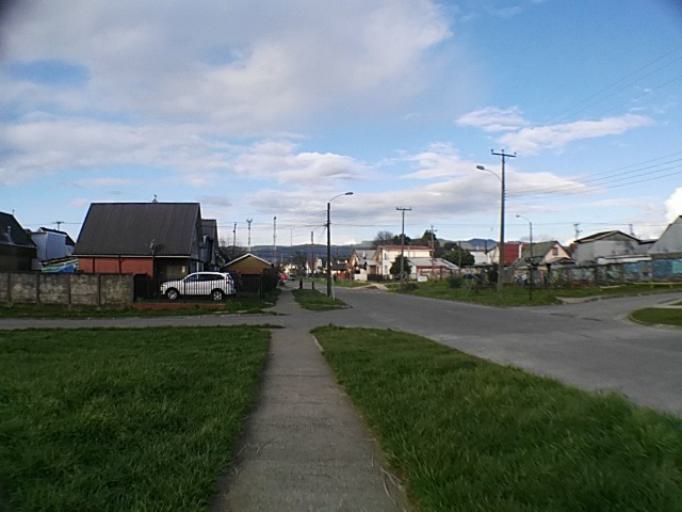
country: CL
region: Los Lagos
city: Las Animas
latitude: -39.8340
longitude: -73.2237
